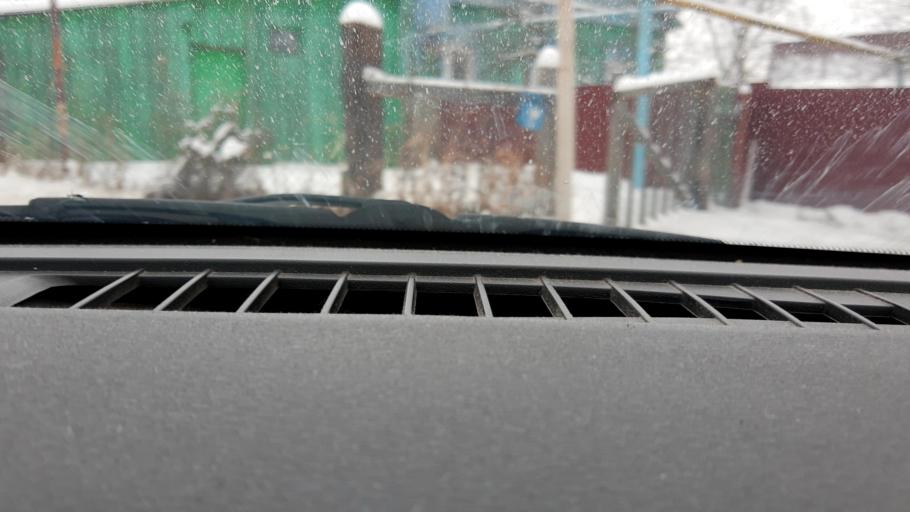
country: RU
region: Nizjnij Novgorod
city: Afonino
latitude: 56.1928
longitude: 44.0662
